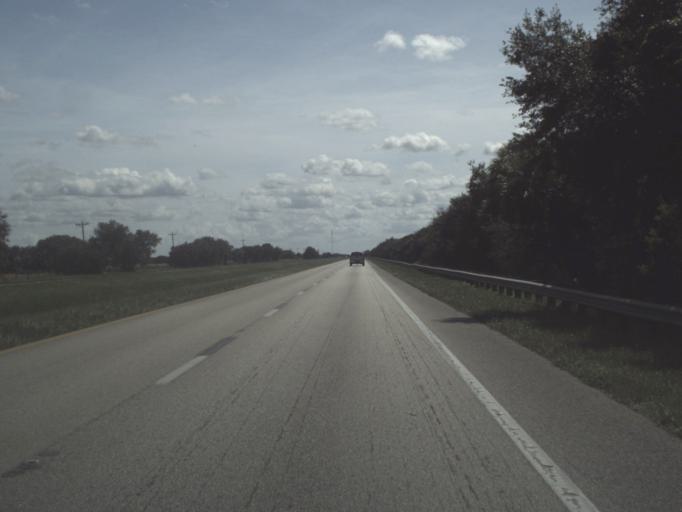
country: US
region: Florida
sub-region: Glades County
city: Moore Haven
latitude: 26.8920
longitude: -81.2366
